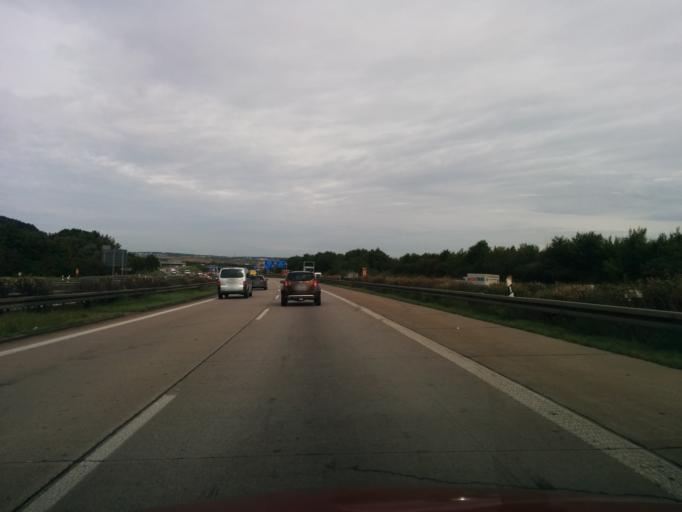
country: DE
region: Baden-Wuerttemberg
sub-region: Regierungsbezirk Stuttgart
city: Leonberg
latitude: 48.7757
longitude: 9.0242
